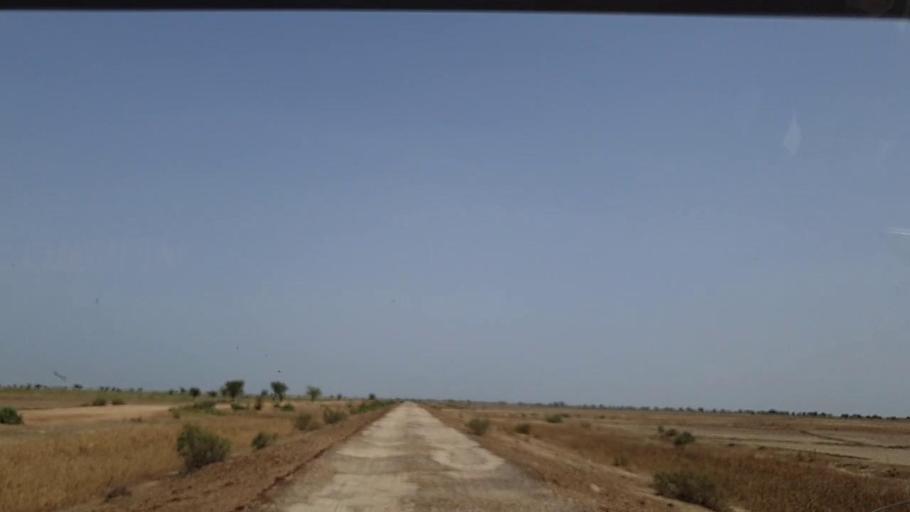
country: PK
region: Sindh
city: Johi
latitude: 26.7808
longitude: 67.6497
